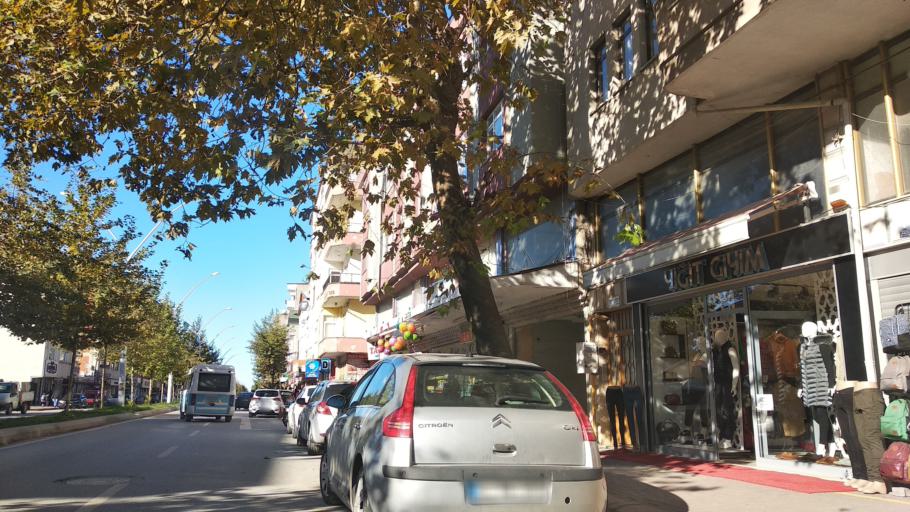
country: TR
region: Sakarya
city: Karasu
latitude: 41.0970
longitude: 30.6926
